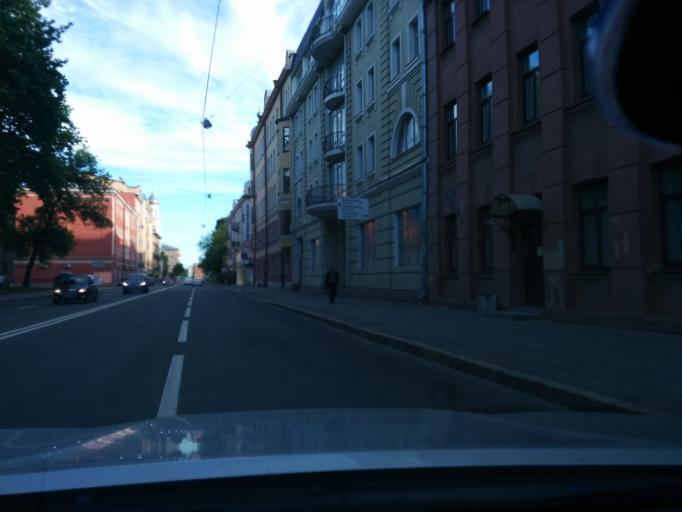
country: RU
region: Leningrad
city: Sampsonievskiy
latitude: 59.9739
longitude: 30.3394
